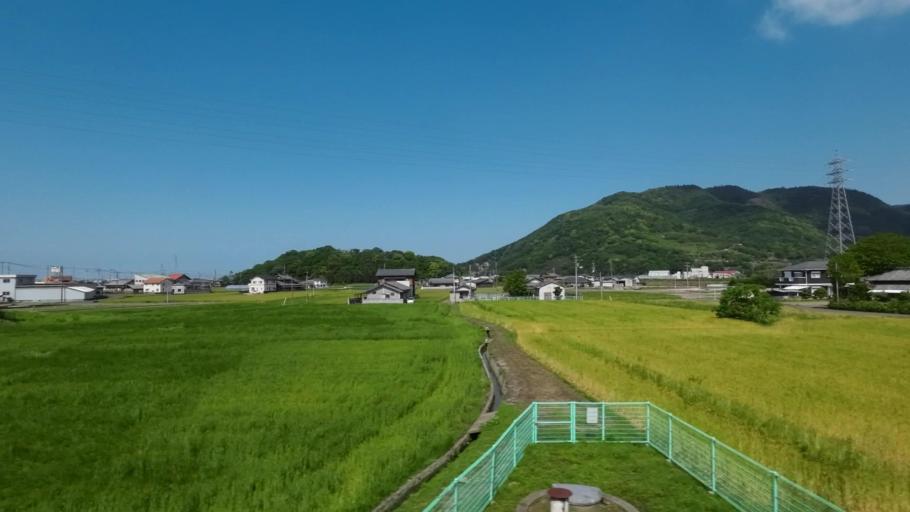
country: JP
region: Kagawa
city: Kan'onjicho
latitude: 34.1368
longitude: 133.6845
